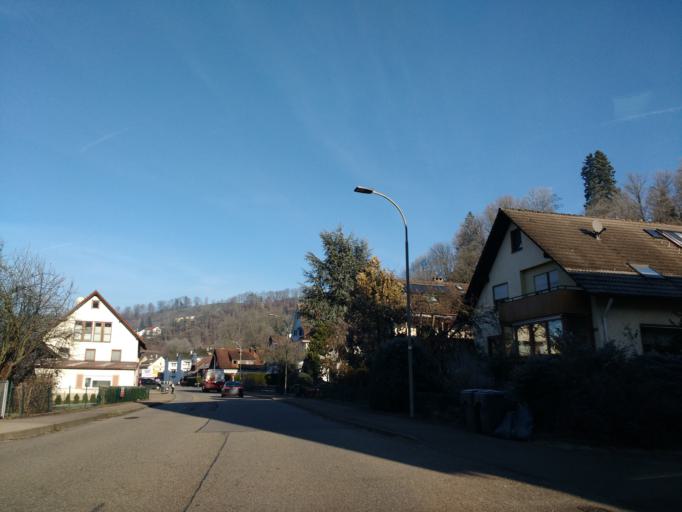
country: DE
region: Baden-Wuerttemberg
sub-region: Freiburg Region
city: Oppenau
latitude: 48.4692
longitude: 8.1636
